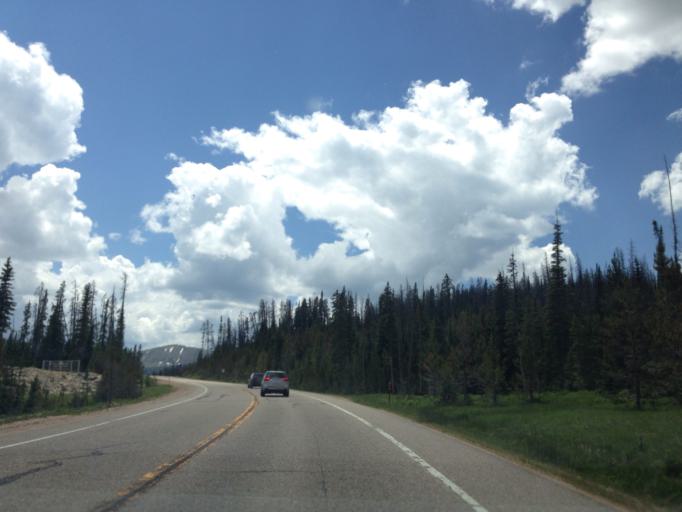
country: US
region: Colorado
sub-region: Larimer County
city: Estes Park
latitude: 40.5612
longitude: -105.8723
